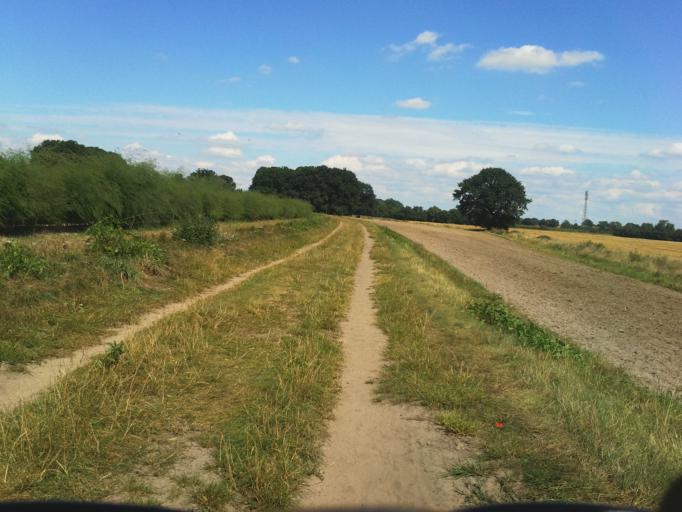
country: DE
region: Lower Saxony
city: Nienburg
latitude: 52.6544
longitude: 9.2393
